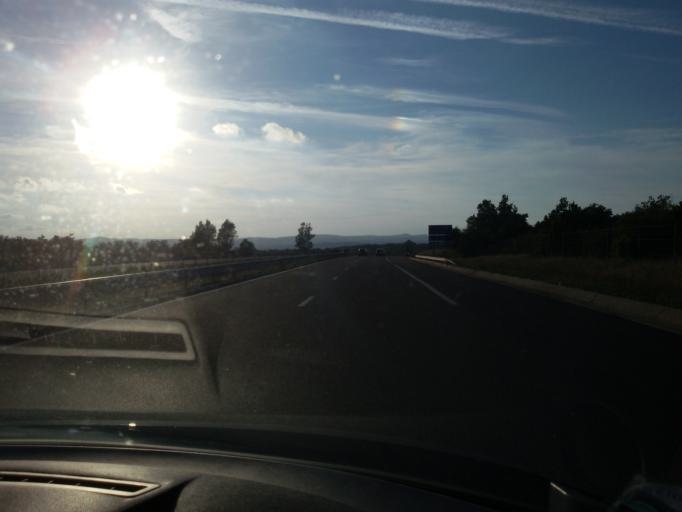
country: FR
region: Midi-Pyrenees
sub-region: Departement de l'Aveyron
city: La Cavalerie
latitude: 43.9211
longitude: 3.2461
